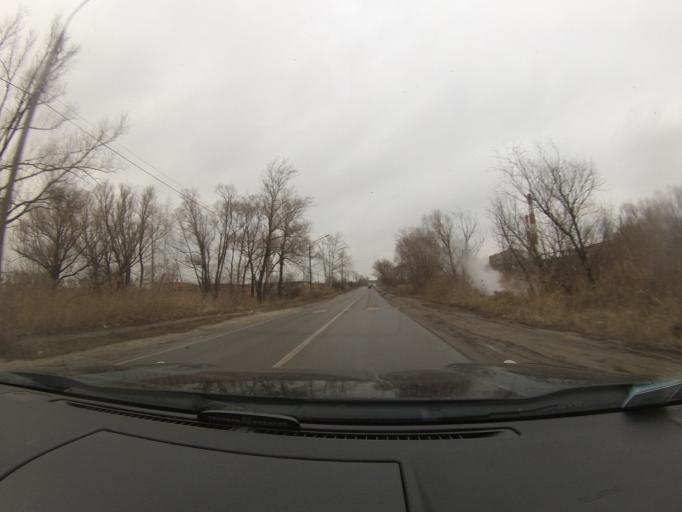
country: RU
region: Moskovskaya
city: Lopatinskiy
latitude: 55.3419
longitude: 38.7312
